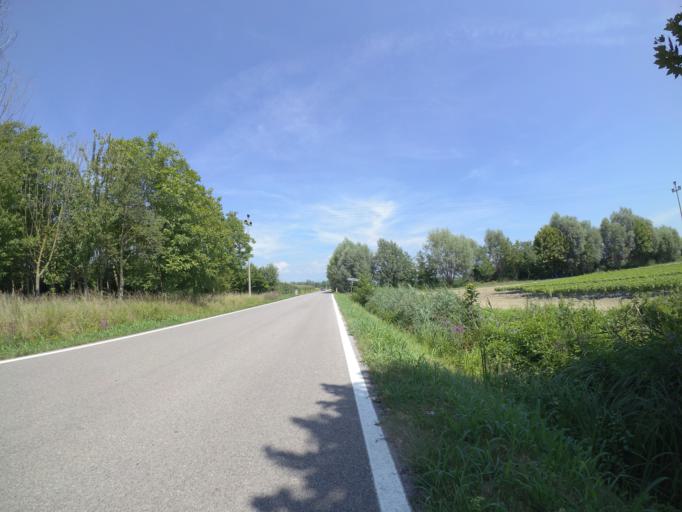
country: IT
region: Friuli Venezia Giulia
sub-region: Provincia di Udine
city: Camino al Tagliamento
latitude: 45.9171
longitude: 12.9648
